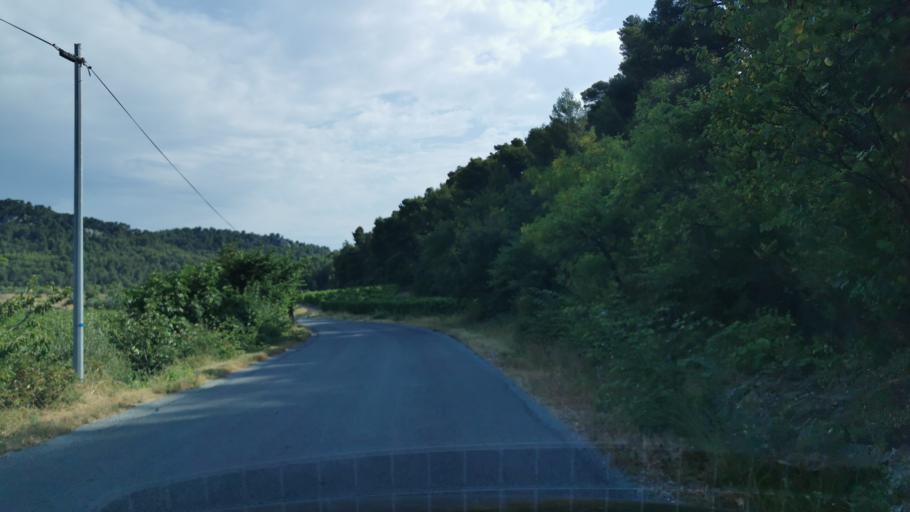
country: FR
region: Languedoc-Roussillon
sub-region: Departement de l'Aude
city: Bize-Minervois
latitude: 43.3201
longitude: 2.8806
